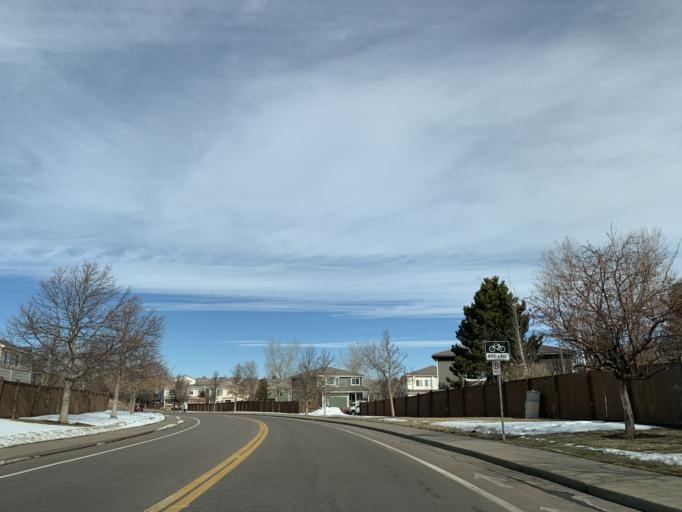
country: US
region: Colorado
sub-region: Douglas County
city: Carriage Club
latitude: 39.5296
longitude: -104.9333
